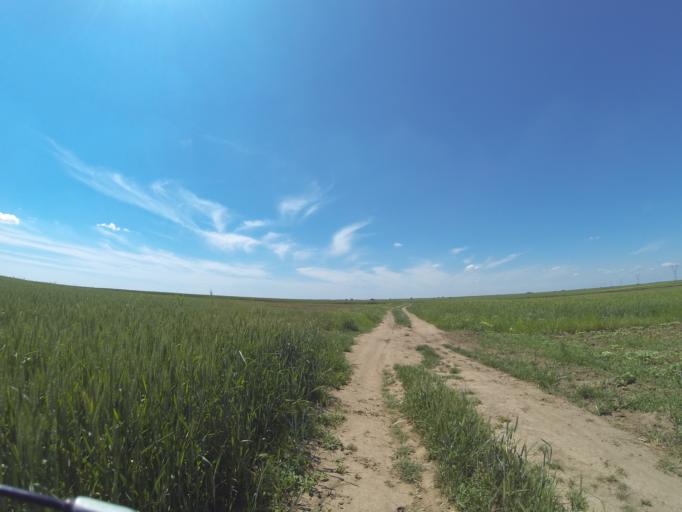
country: RO
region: Dolj
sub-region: Comuna Leu
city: Leu
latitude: 44.2103
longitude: 24.0350
